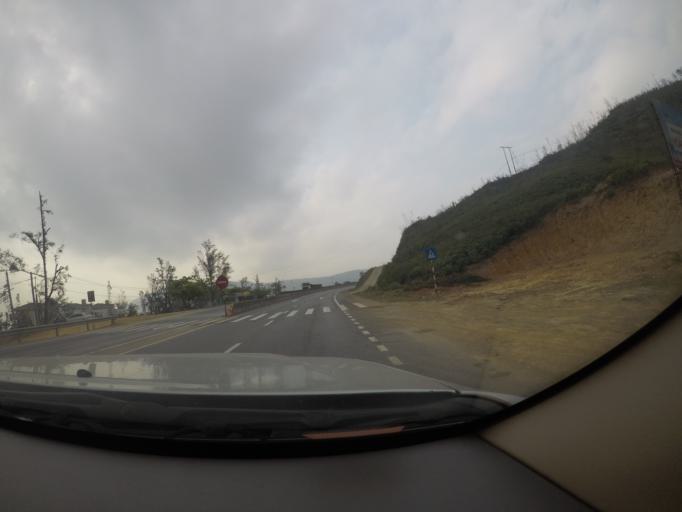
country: VN
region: Ha Tinh
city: Ky Anh
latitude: 17.9838
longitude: 106.4811
